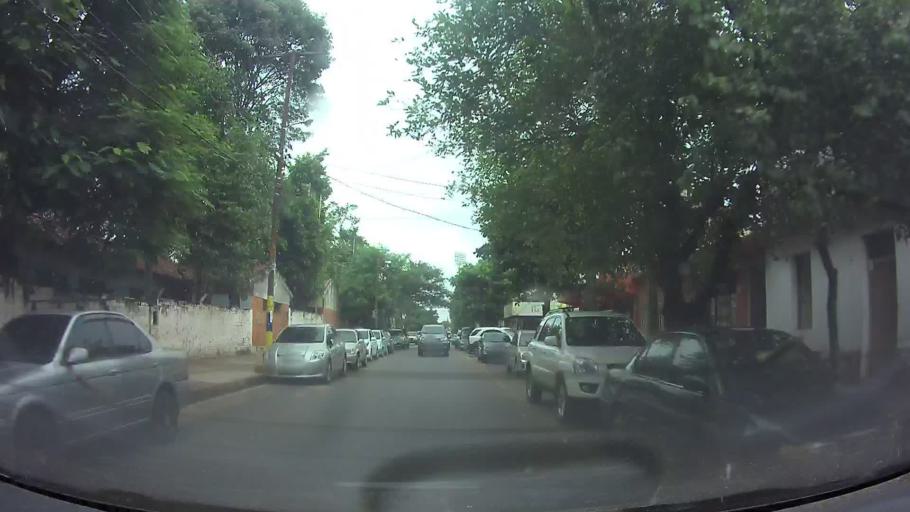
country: PY
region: Central
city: San Lorenzo
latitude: -25.2708
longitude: -57.4919
